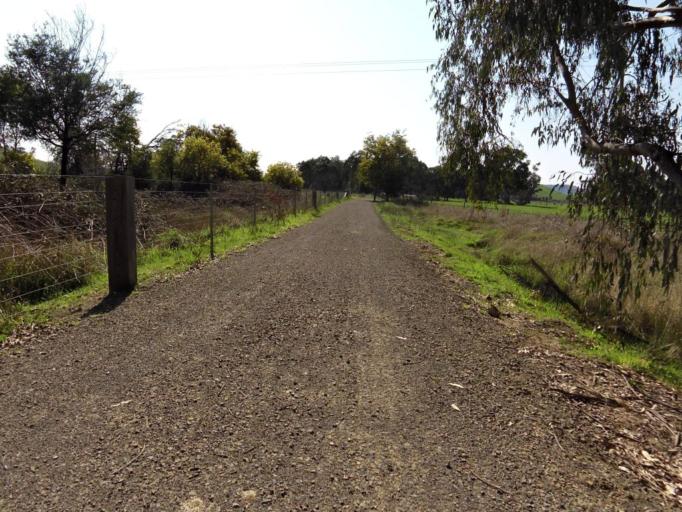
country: AU
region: Victoria
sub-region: Murrindindi
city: Alexandra
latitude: -37.1532
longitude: 145.5772
